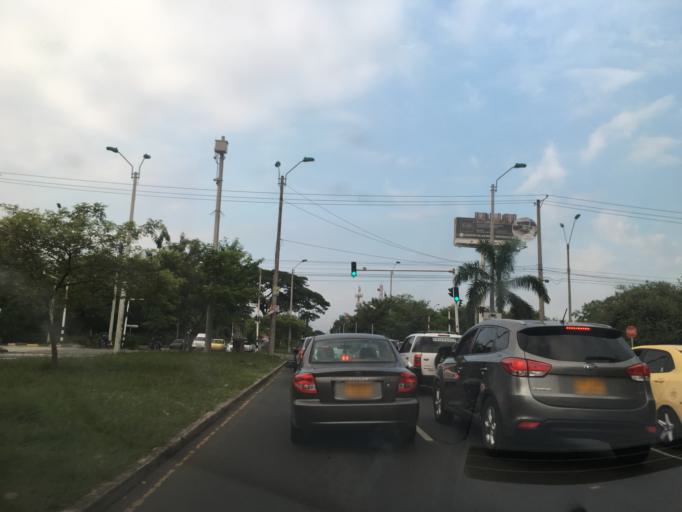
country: CO
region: Valle del Cauca
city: Cali
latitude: 3.3933
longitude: -76.5281
